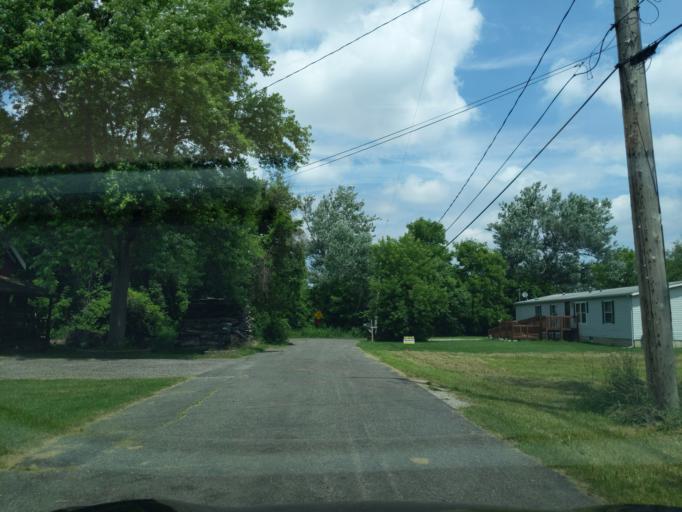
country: US
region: Michigan
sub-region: Ingham County
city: Edgemont Park
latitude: 42.7710
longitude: -84.5632
